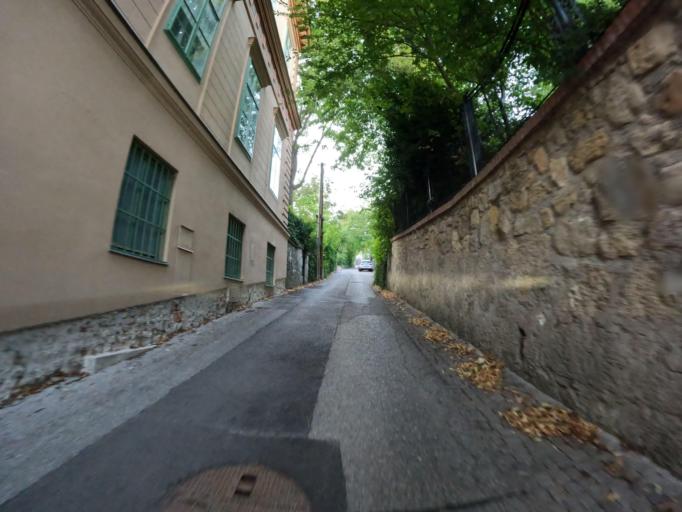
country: AT
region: Lower Austria
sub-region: Politischer Bezirk Baden
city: Baden
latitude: 48.0092
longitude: 16.2164
